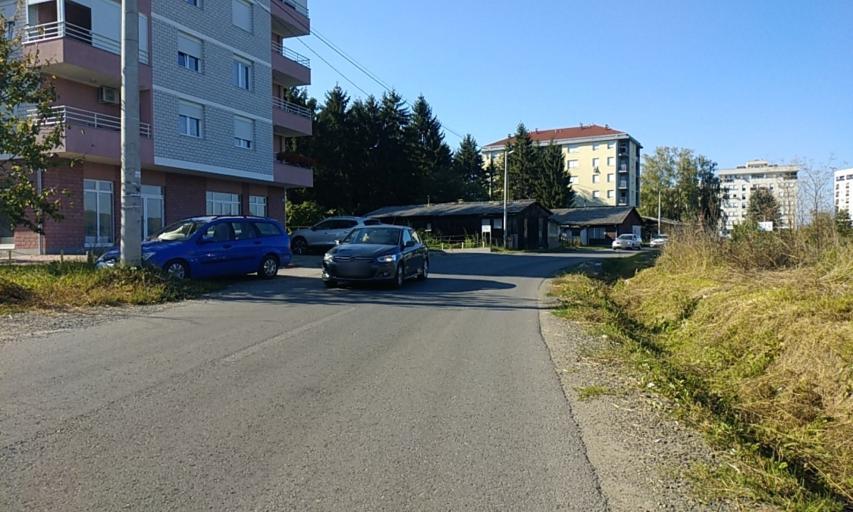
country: BA
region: Republika Srpska
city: Starcevica
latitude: 44.7716
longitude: 17.2183
